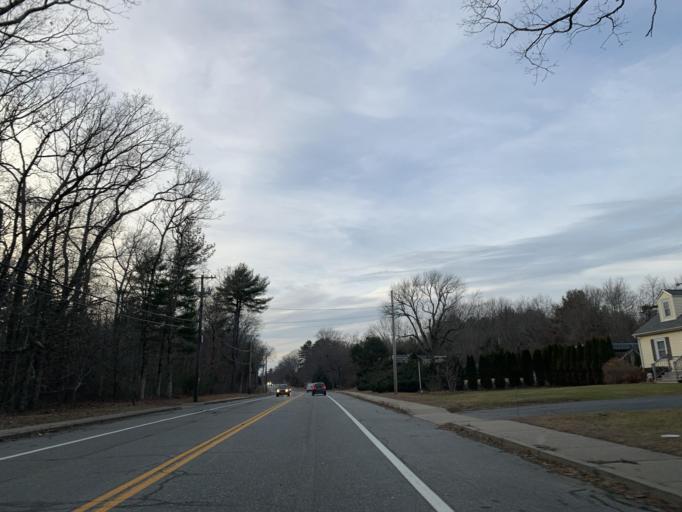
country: US
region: Rhode Island
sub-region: Providence County
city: Chepachet
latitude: 41.9177
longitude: -71.6818
